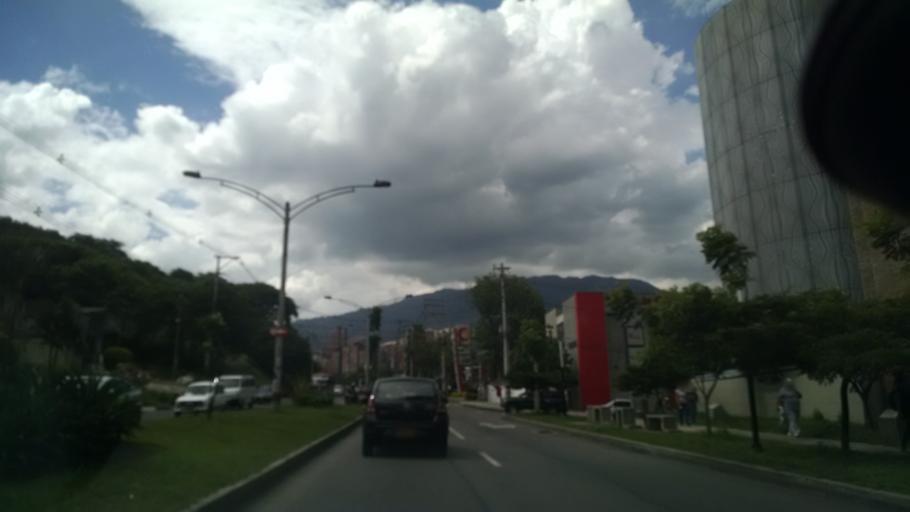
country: CO
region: Antioquia
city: Medellin
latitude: 6.2708
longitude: -75.5775
